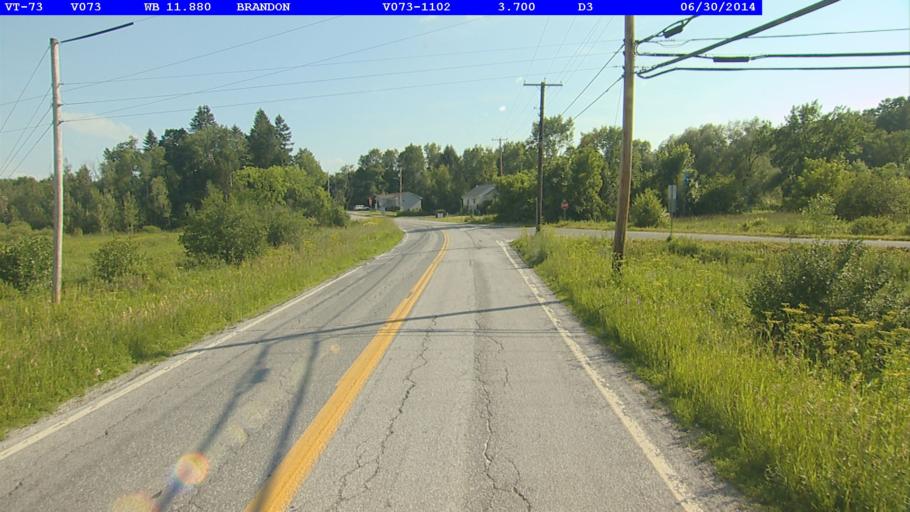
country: US
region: Vermont
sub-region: Rutland County
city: Brandon
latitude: 43.8033
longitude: -73.0801
